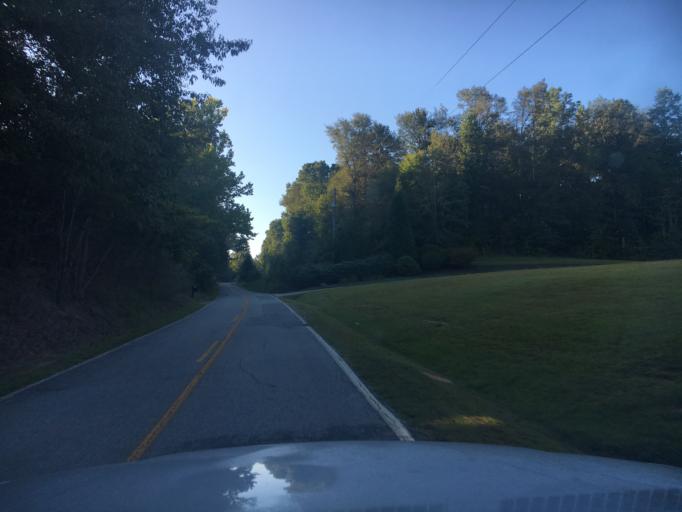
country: US
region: South Carolina
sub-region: Spartanburg County
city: Woodruff
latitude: 34.7680
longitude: -81.9637
